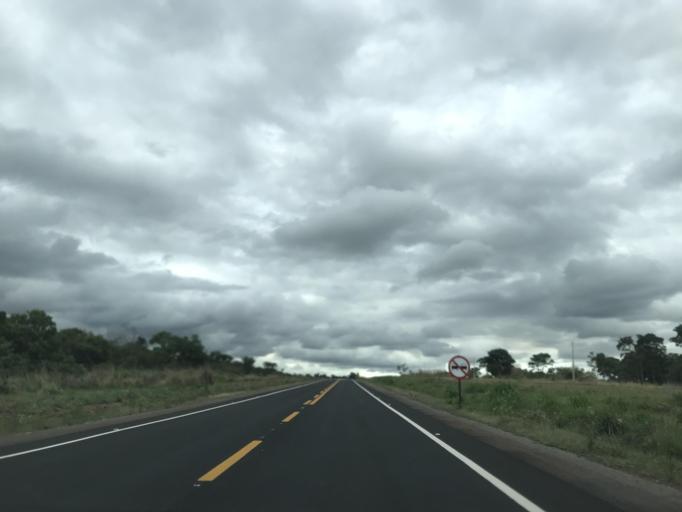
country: BR
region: Goias
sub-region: Caldas Novas
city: Caldas Novas
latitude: -17.7048
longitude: -48.7349
